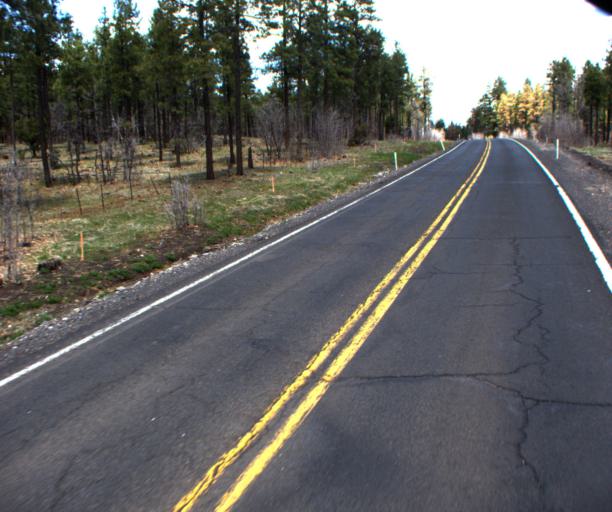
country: US
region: Arizona
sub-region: Coconino County
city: Kachina Village
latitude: 35.0824
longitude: -111.7295
